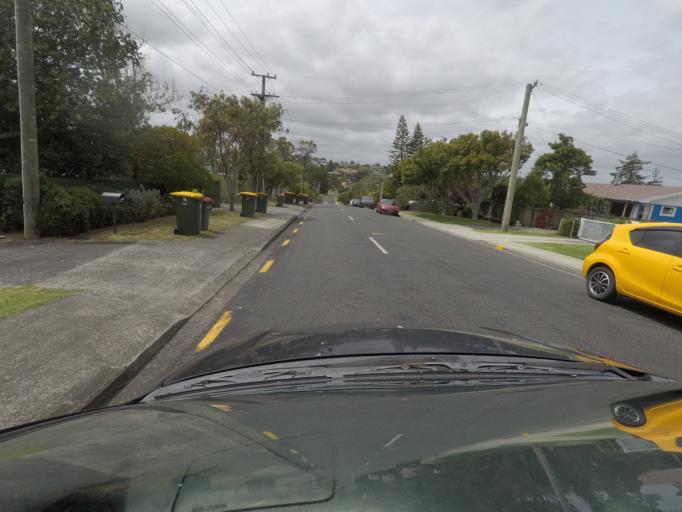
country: NZ
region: Auckland
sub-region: Auckland
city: Pakuranga
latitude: -36.8908
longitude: 174.9377
